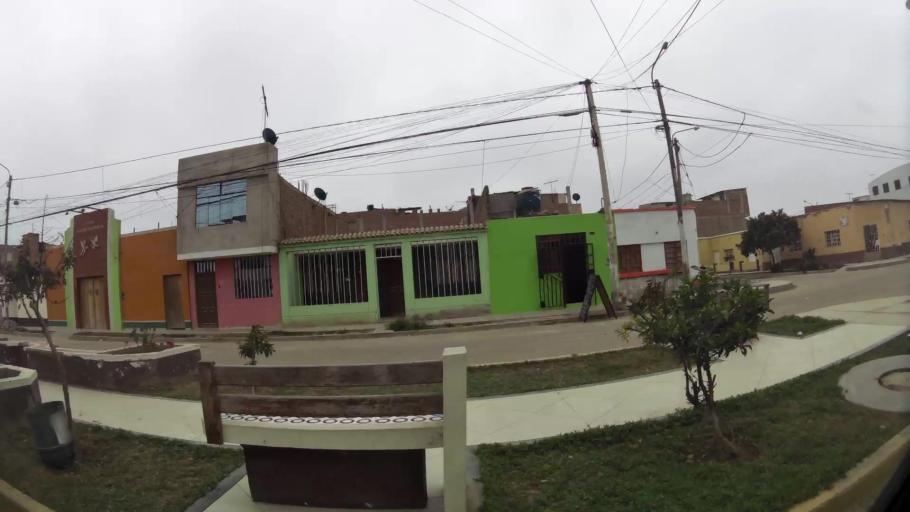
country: PE
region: La Libertad
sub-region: Provincia de Trujillo
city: Buenos Aires
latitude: -8.1447
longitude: -79.0529
